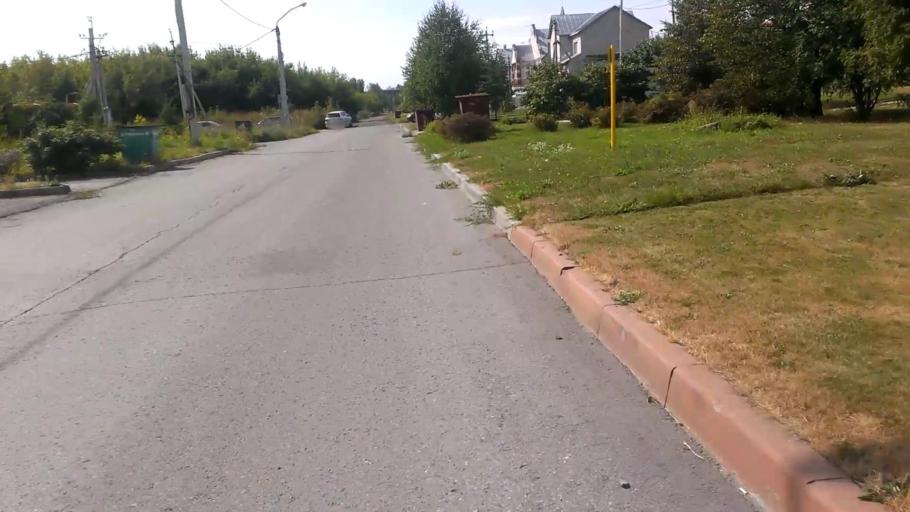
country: RU
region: Altai Krai
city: Novosilikatnyy
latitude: 53.3529
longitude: 83.6509
